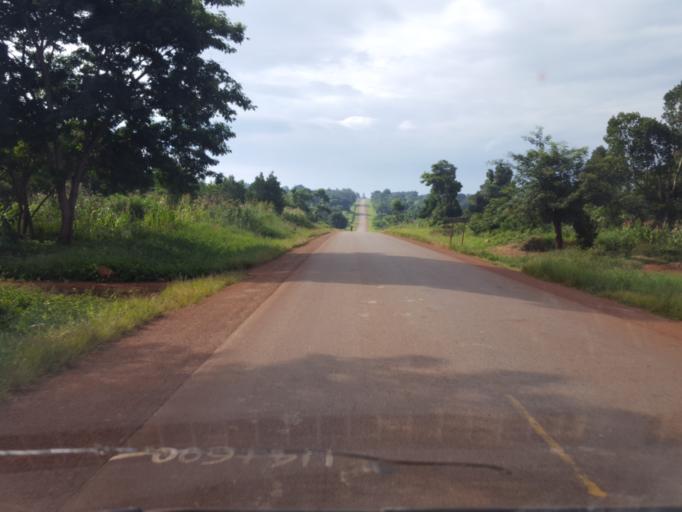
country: UG
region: Western Region
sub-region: Hoima District
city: Hoima
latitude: 1.2456
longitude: 31.5257
